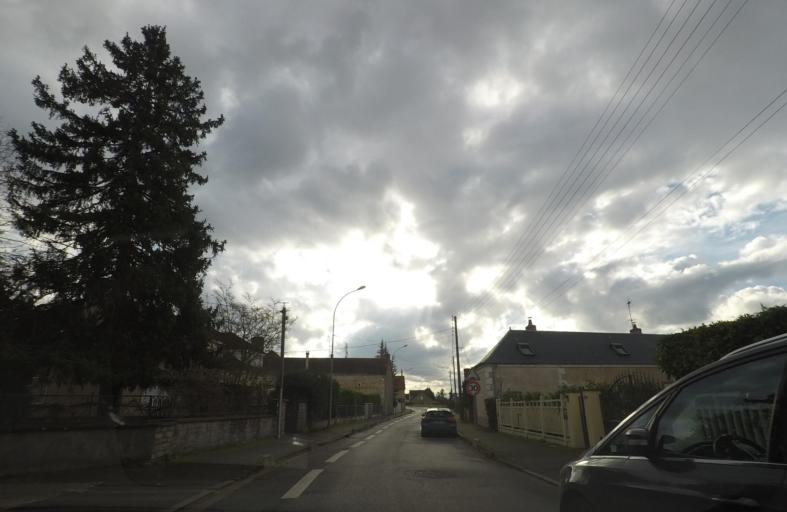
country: FR
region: Centre
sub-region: Departement du Cher
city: Bourges
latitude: 47.0681
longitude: 2.3991
